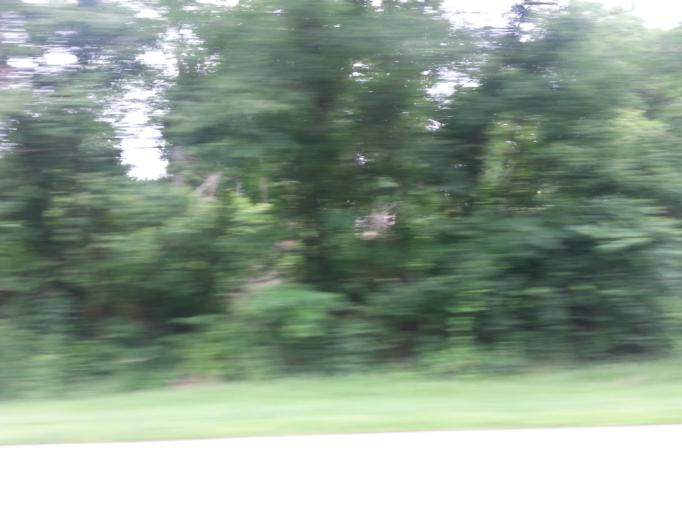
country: US
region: Ohio
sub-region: Brown County
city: Mount Orab
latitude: 38.9568
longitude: -83.9129
